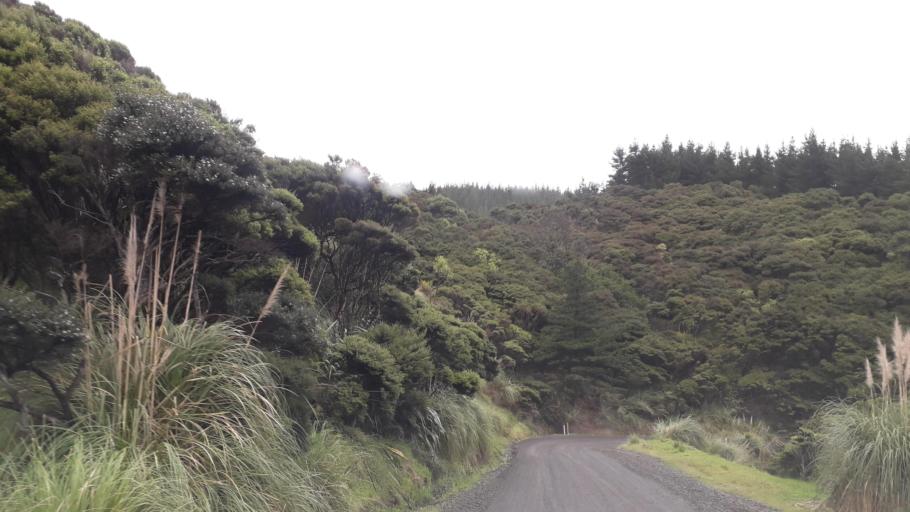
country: NZ
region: Northland
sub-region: Far North District
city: Ahipara
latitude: -35.4413
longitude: 173.3033
